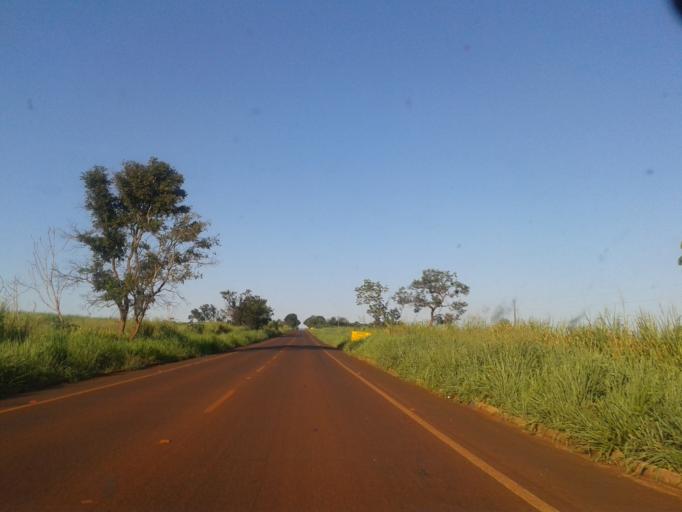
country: BR
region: Minas Gerais
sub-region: Capinopolis
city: Capinopolis
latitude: -18.7024
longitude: -49.6670
